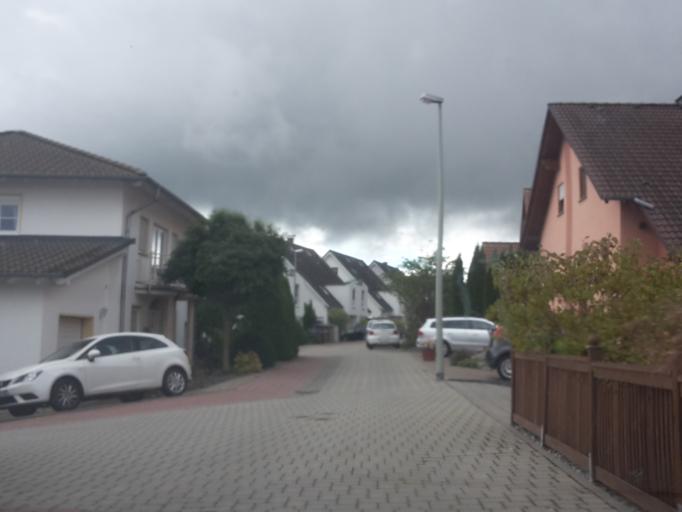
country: DE
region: Hesse
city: Bad Camberg
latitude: 50.2753
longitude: 8.1922
